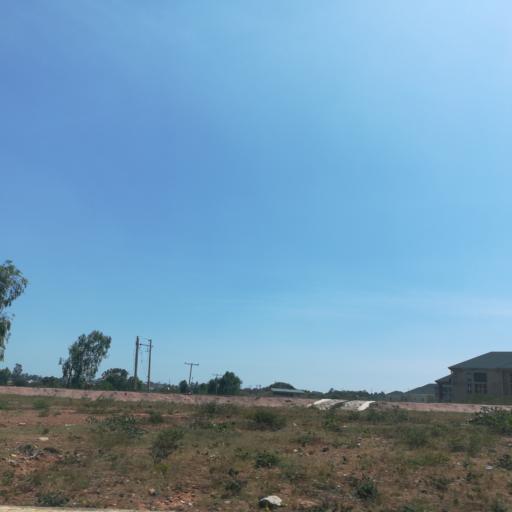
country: NG
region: Plateau
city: Bukuru
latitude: 9.8233
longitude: 8.8804
